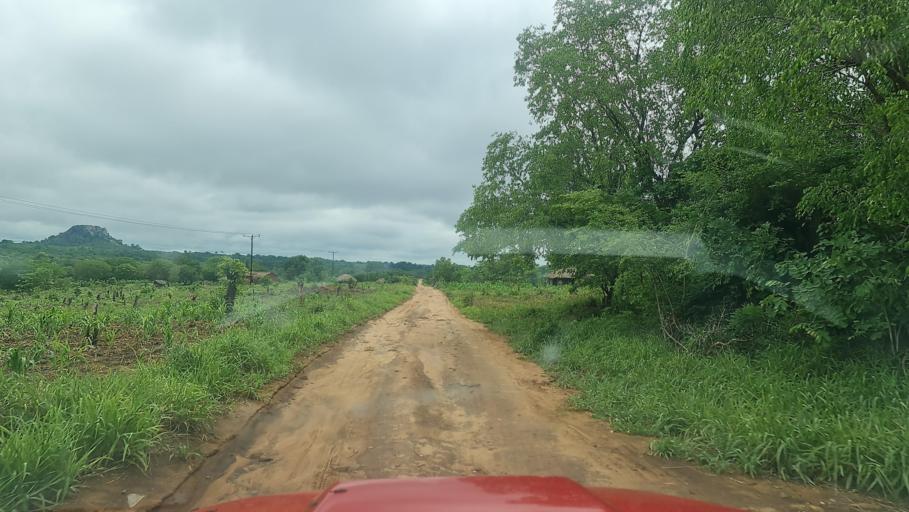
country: MW
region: Southern Region
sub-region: Nsanje District
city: Nsanje
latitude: -17.1924
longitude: 35.8622
